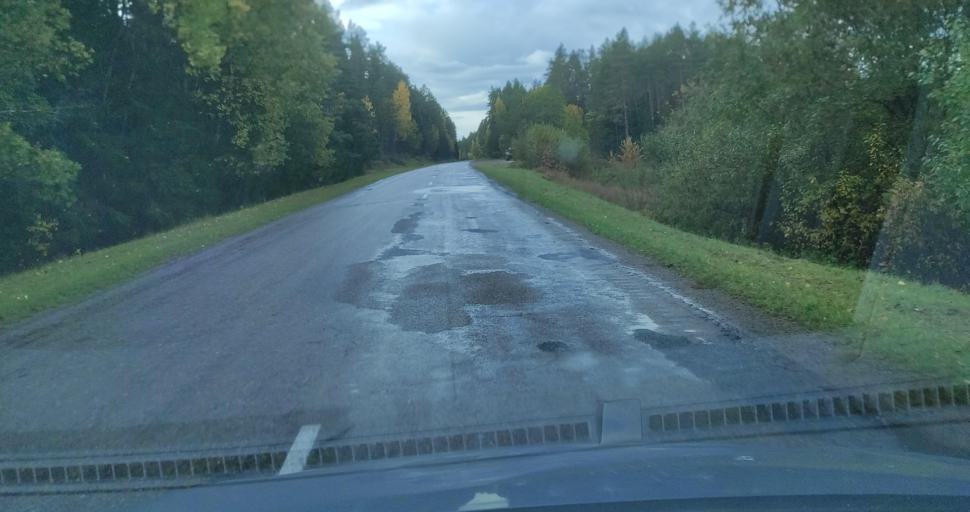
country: LV
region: Skrunda
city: Skrunda
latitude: 56.6557
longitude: 22.0188
